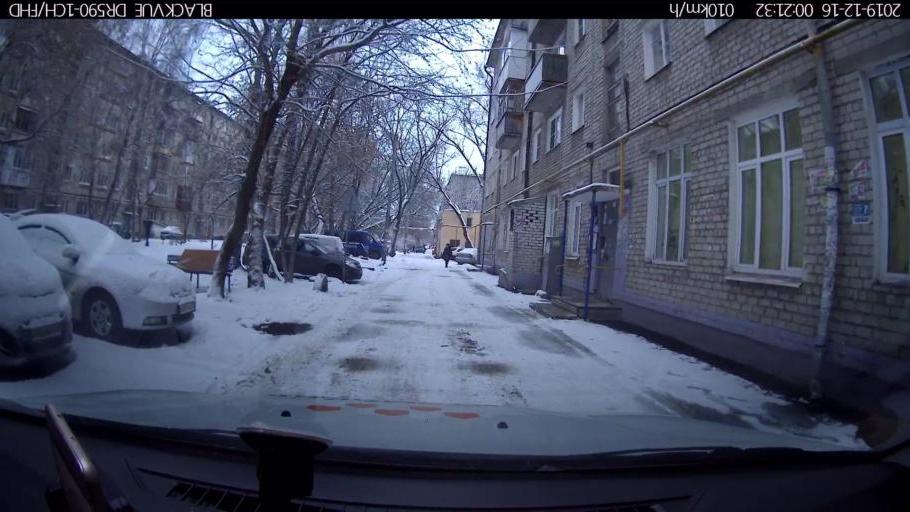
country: RU
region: Nizjnij Novgorod
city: Nizhniy Novgorod
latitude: 56.3221
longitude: 43.8860
